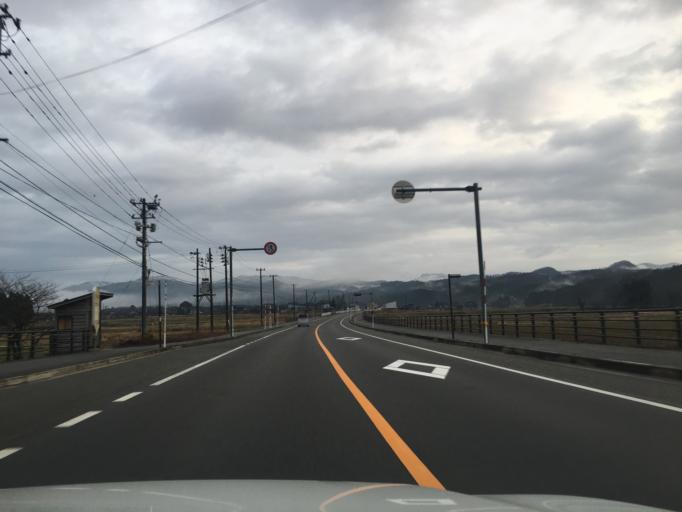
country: JP
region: Niigata
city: Murakami
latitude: 38.3191
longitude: 139.5519
